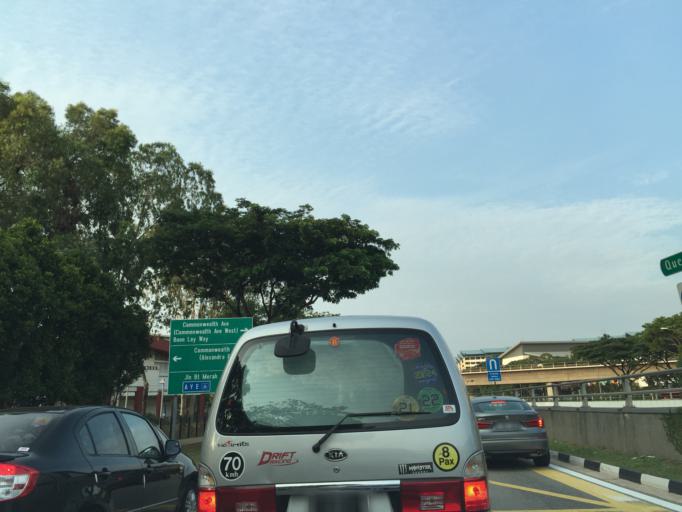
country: SG
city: Singapore
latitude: 1.3016
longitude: 103.8013
